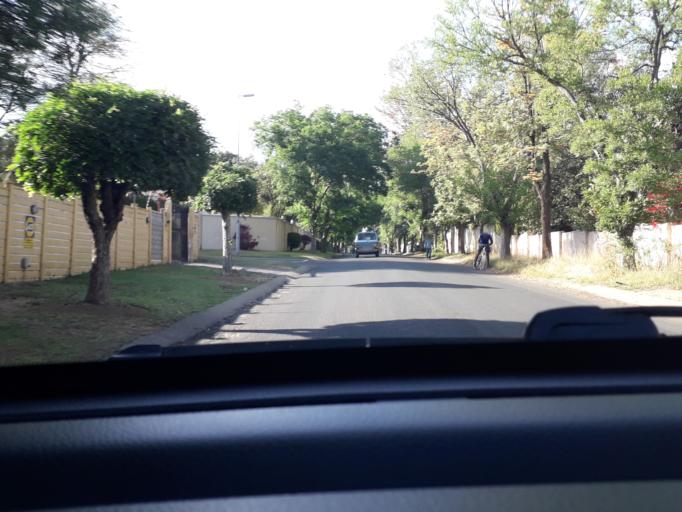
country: ZA
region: Gauteng
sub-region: City of Johannesburg Metropolitan Municipality
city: Modderfontein
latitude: -26.0712
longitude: 28.0783
